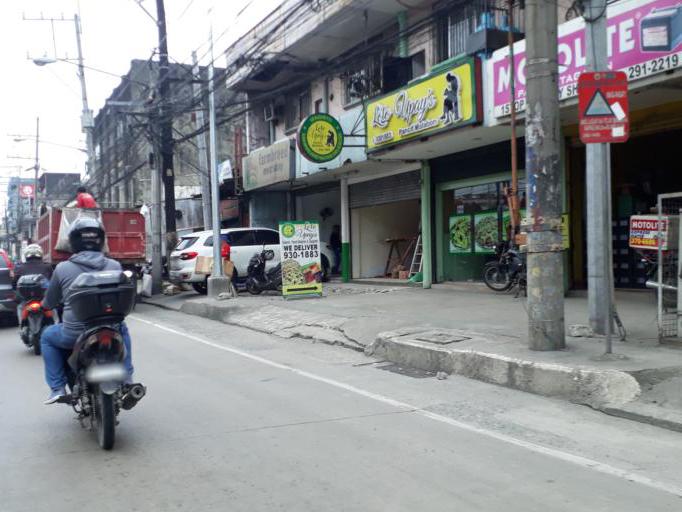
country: PH
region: Metro Manila
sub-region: Caloocan City
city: Niugan
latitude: 14.6751
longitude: 120.9812
